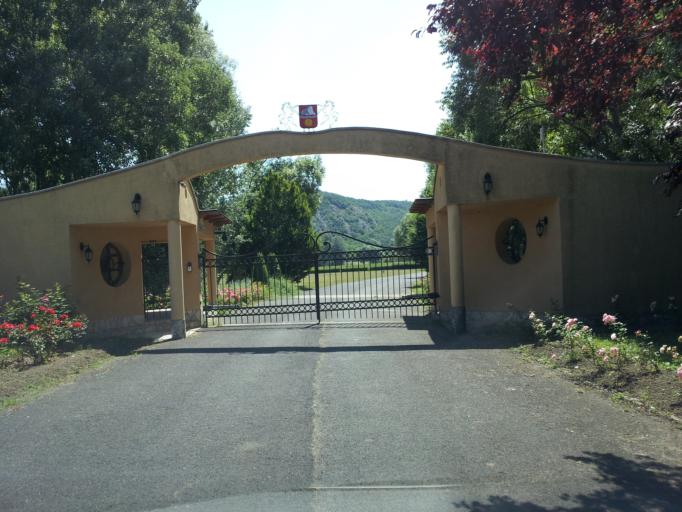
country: HU
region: Fejer
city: Szarliget
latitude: 47.5207
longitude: 18.5476
